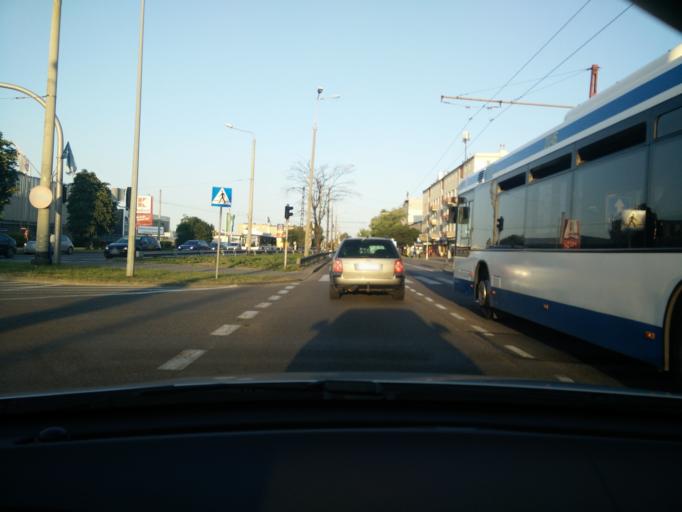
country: PL
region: Pomeranian Voivodeship
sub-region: Gdynia
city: Gdynia
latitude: 54.5292
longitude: 18.5033
